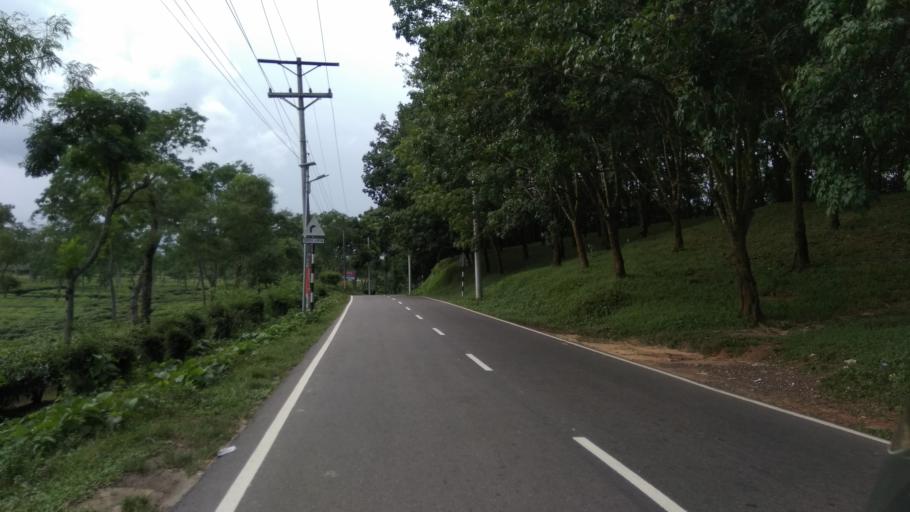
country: IN
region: Tripura
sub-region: Dhalai
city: Kamalpur
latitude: 24.3000
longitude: 91.7562
